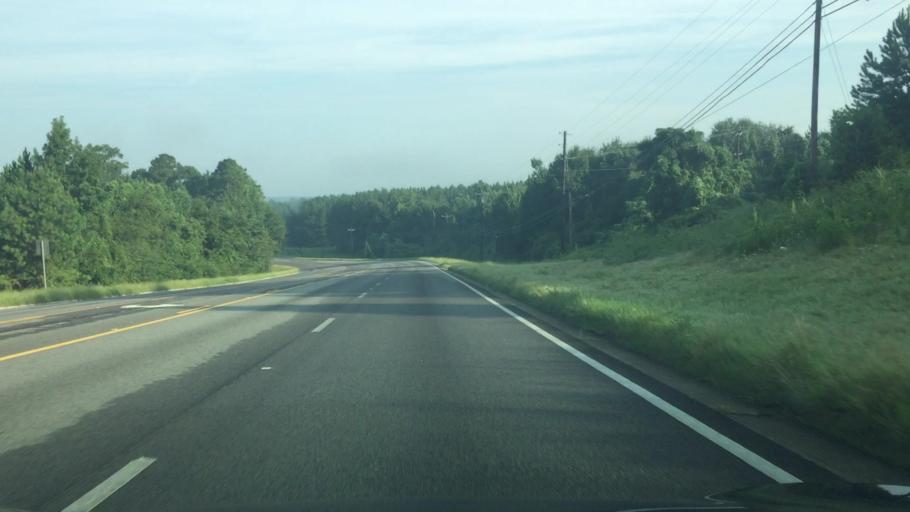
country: US
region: Alabama
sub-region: Covington County
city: Andalusia
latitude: 31.3297
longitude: -86.5128
